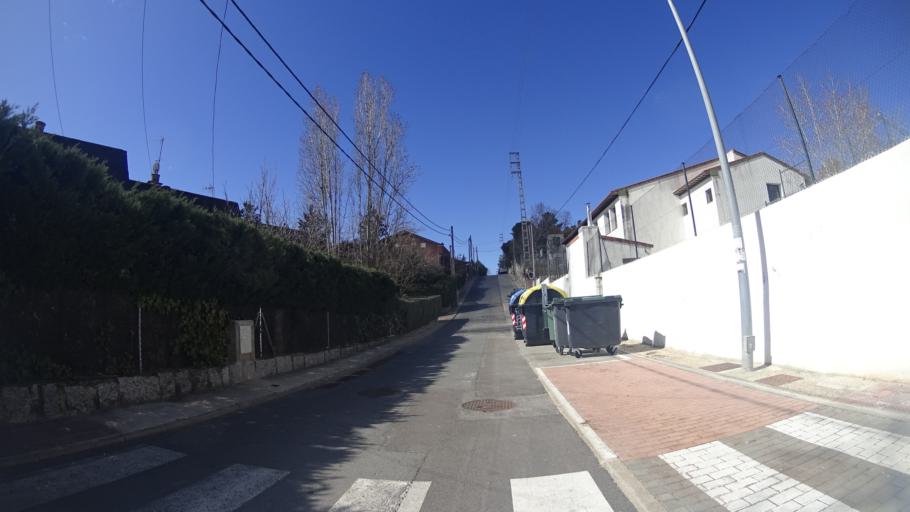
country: ES
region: Madrid
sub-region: Provincia de Madrid
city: Las Matas
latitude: 40.5639
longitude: -3.9000
